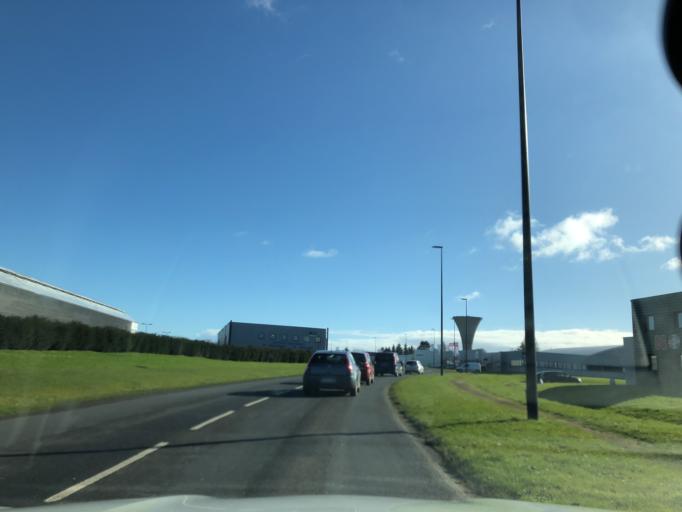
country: FR
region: Lower Normandy
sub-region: Departement du Calvados
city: Epron
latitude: 49.2162
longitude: -0.3488
